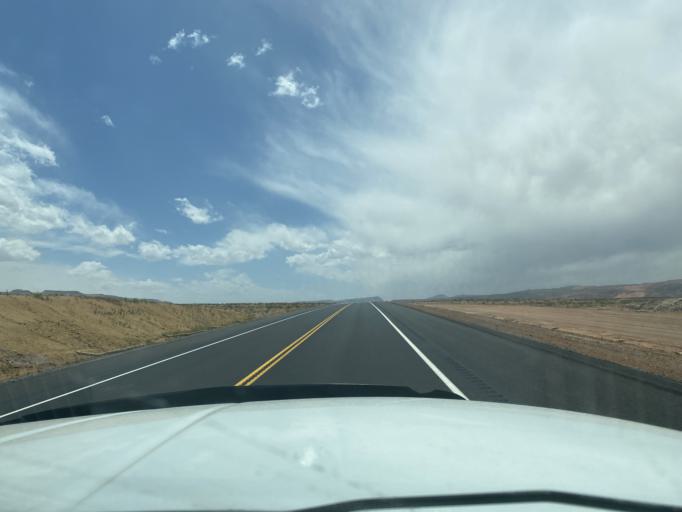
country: US
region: Utah
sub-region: Washington County
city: Hurricane
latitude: 37.1550
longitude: -113.3459
